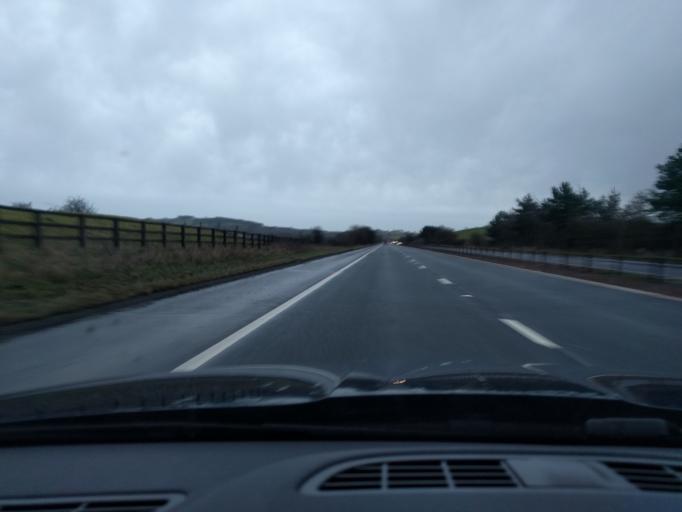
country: GB
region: Scotland
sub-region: Falkirk
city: Bo'ness
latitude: 55.9856
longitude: -3.6540
